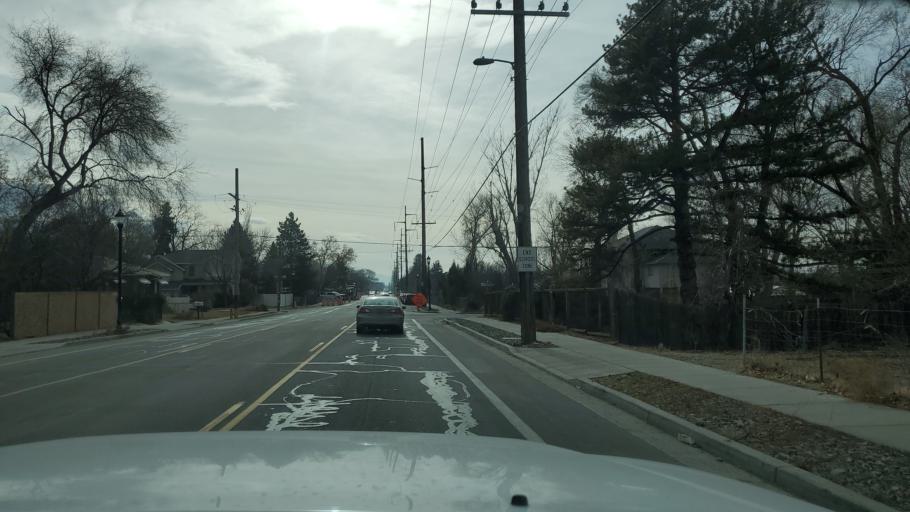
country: US
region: Utah
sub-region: Salt Lake County
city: Millcreek
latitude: 40.6968
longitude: -111.8656
